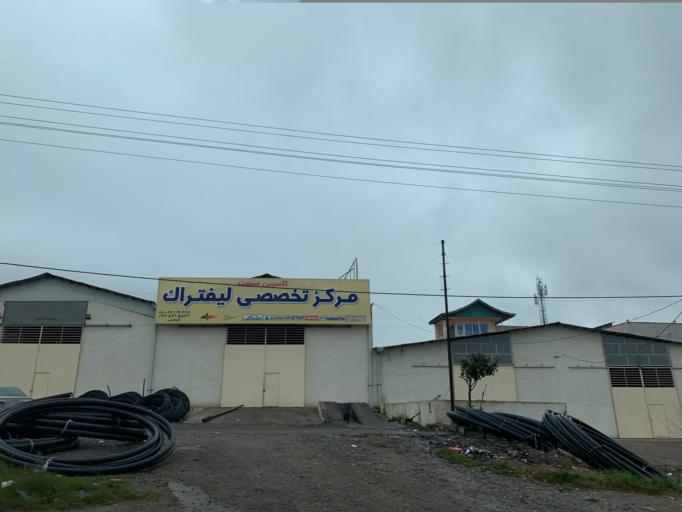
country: IR
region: Mazandaran
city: Amol
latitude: 36.4041
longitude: 52.3470
